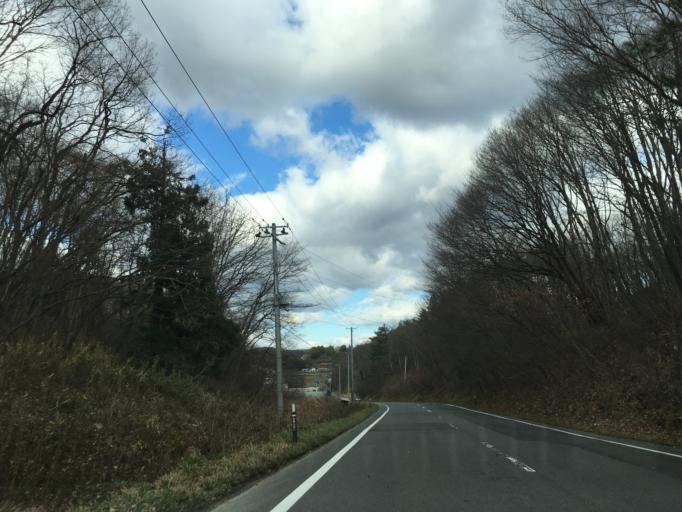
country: JP
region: Fukushima
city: Sukagawa
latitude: 37.3357
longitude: 140.4407
